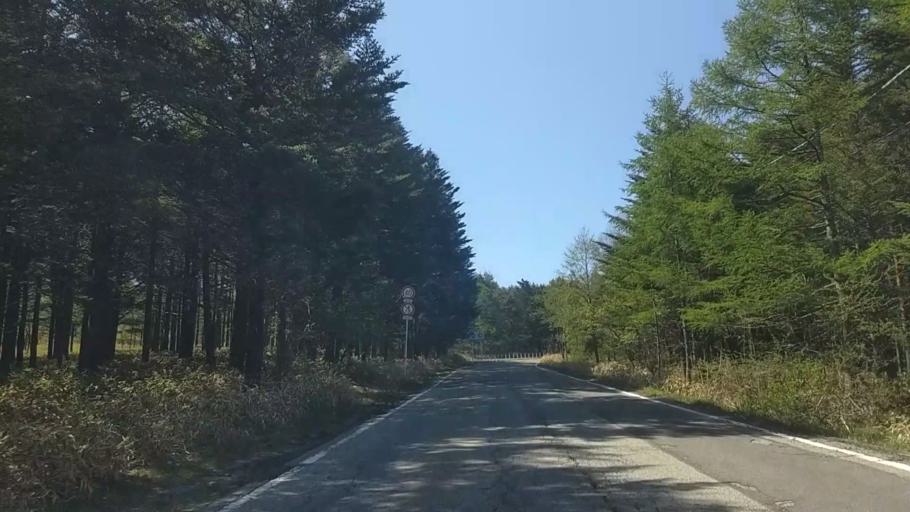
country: JP
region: Yamanashi
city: Nirasaki
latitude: 35.9416
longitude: 138.4204
